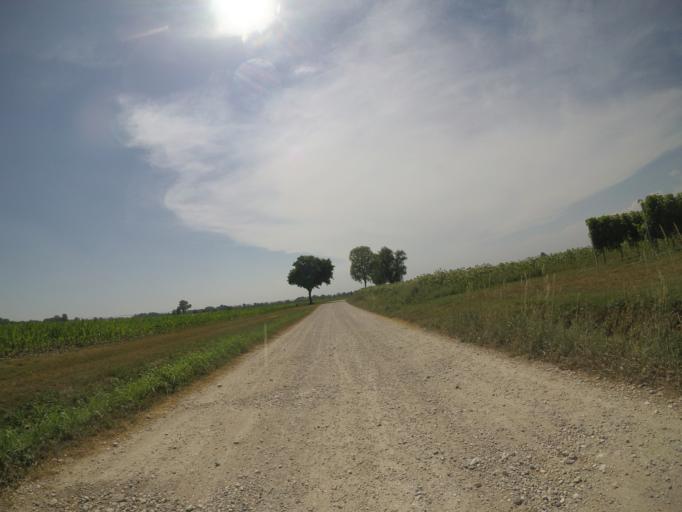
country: IT
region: Friuli Venezia Giulia
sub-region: Provincia di Udine
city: Camino al Tagliamento
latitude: 45.9270
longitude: 12.9327
